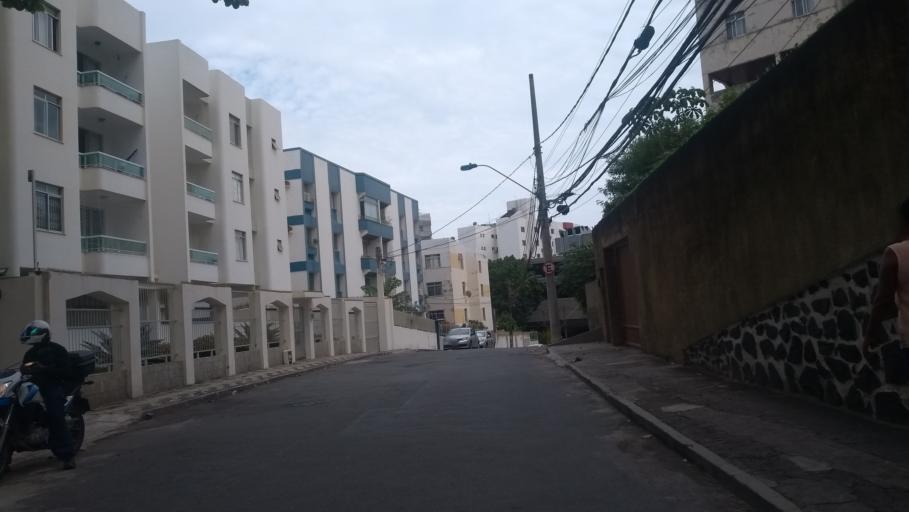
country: BR
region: Bahia
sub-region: Salvador
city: Salvador
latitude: -12.9958
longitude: -38.4463
